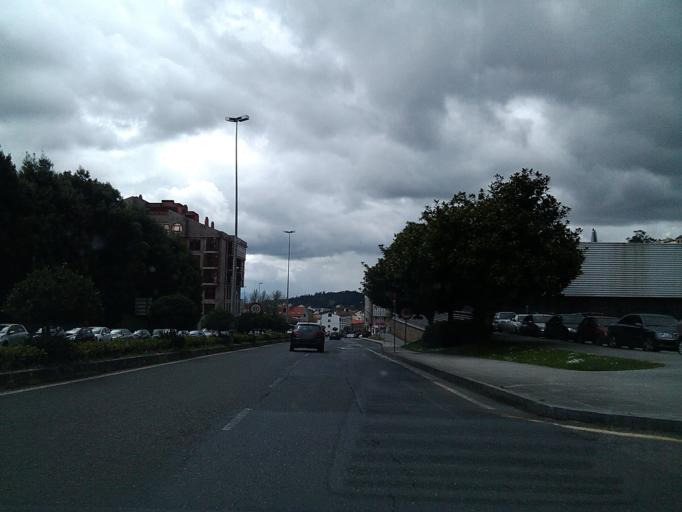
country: ES
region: Galicia
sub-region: Provincia da Coruna
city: Santiago de Compostela
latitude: 42.8884
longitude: -8.5326
